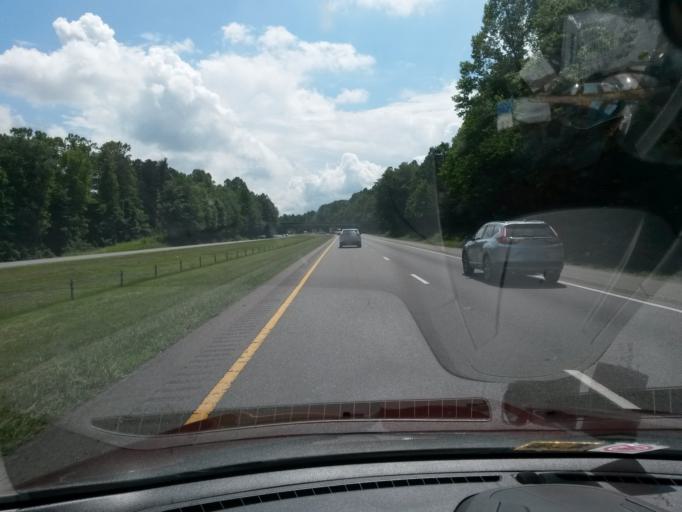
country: US
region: North Carolina
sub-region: Surry County
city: Dobson
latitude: 36.4628
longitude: -80.7636
